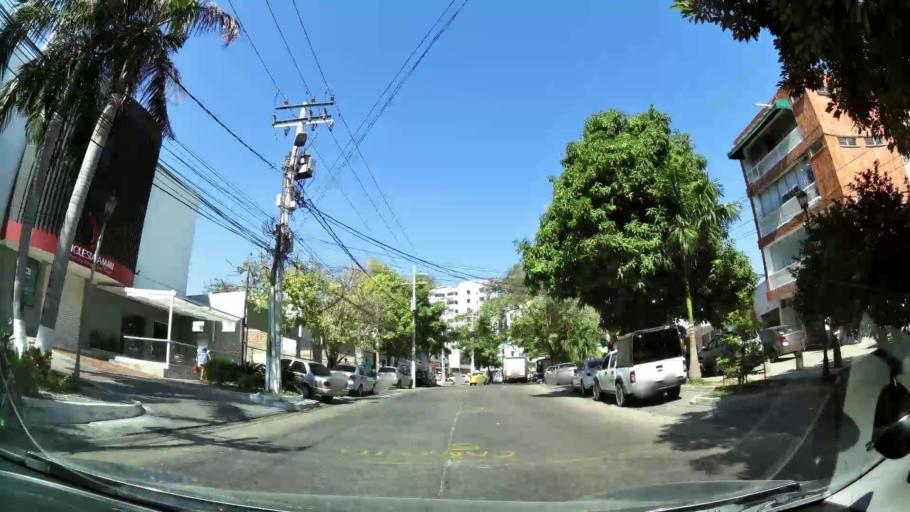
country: CO
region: Atlantico
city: Barranquilla
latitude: 10.9977
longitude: -74.8017
